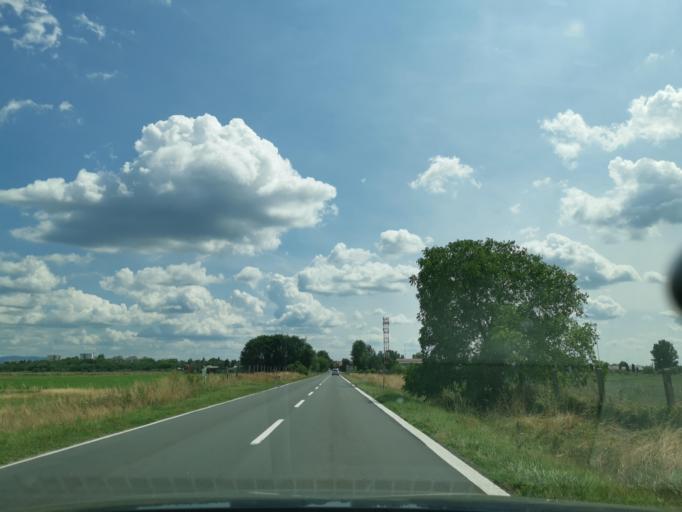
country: SK
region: Bratislavsky
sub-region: Okres Malacky
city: Malacky
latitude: 48.5142
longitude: 16.9941
